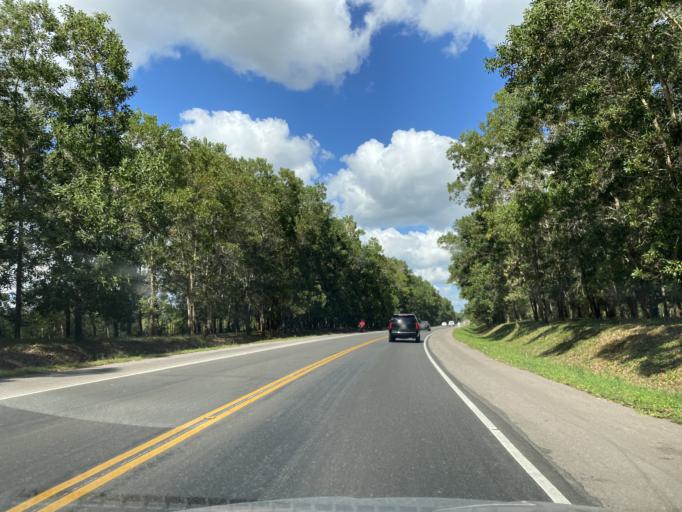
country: DO
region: Monte Plata
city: Monte Plata
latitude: 18.7502
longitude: -69.7661
